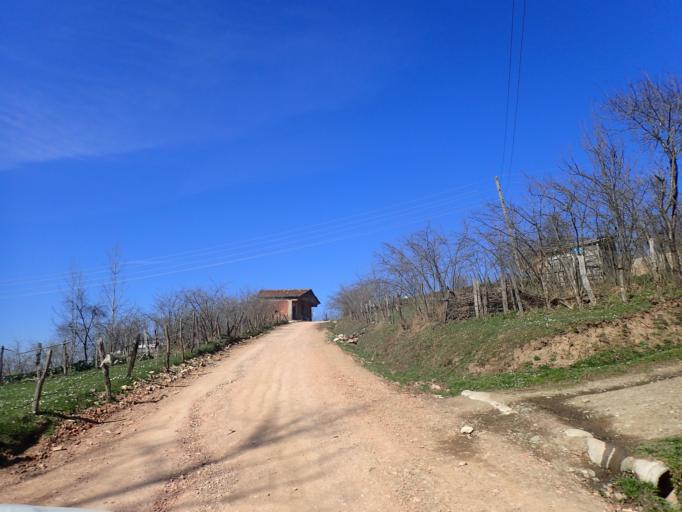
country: TR
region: Ordu
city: Catalpinar
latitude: 40.8646
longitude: 37.4973
